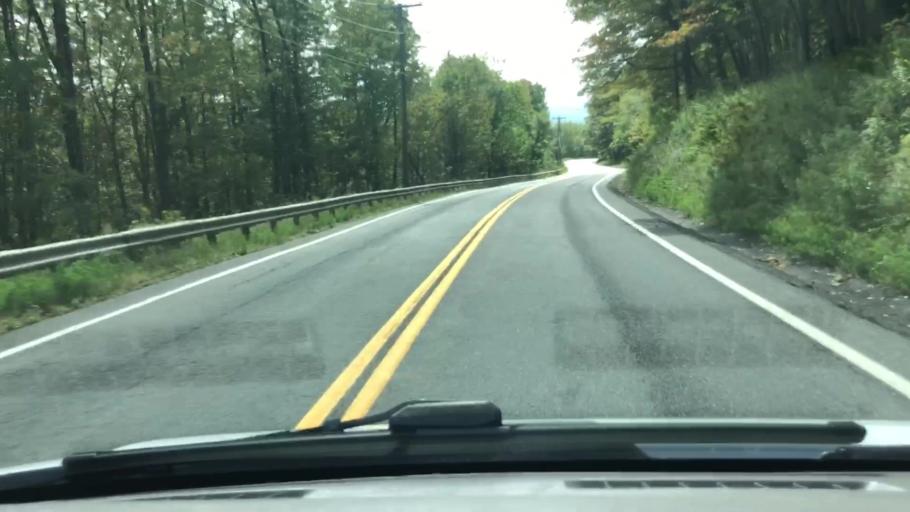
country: US
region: Massachusetts
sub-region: Berkshire County
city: North Adams
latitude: 42.6860
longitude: -73.0195
